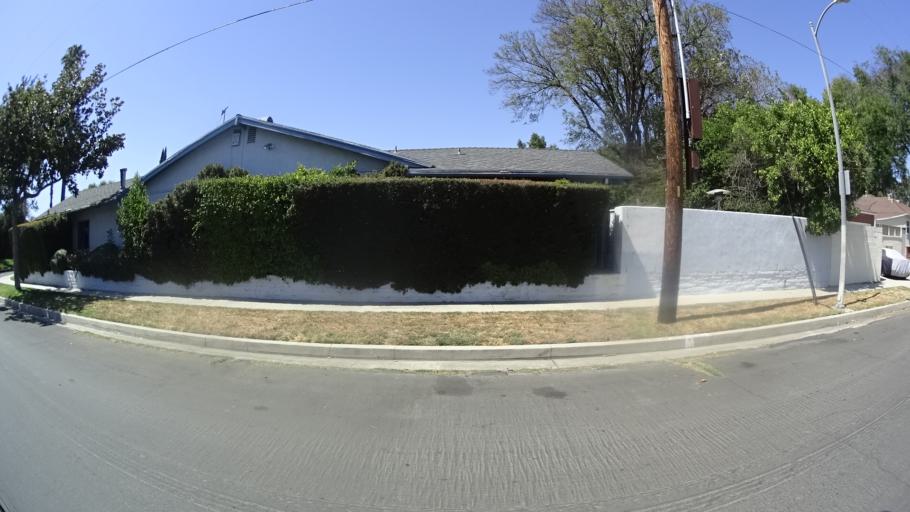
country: US
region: California
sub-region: Los Angeles County
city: Van Nuys
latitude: 34.1893
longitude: -118.4966
